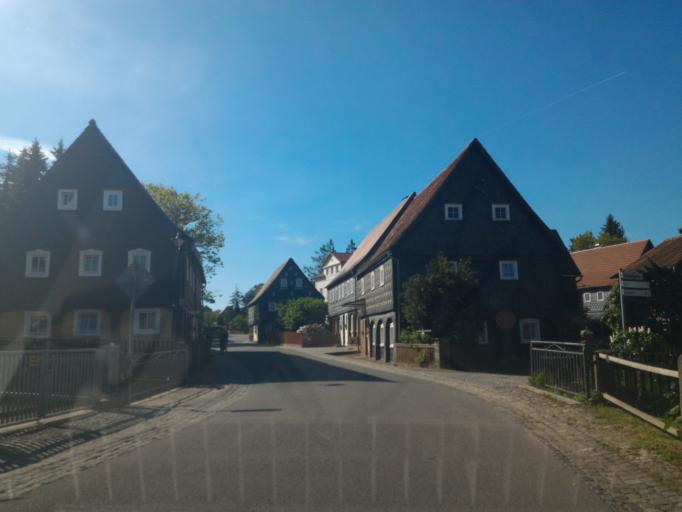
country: DE
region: Saxony
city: Niedercunnersdorf
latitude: 51.0344
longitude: 14.6694
